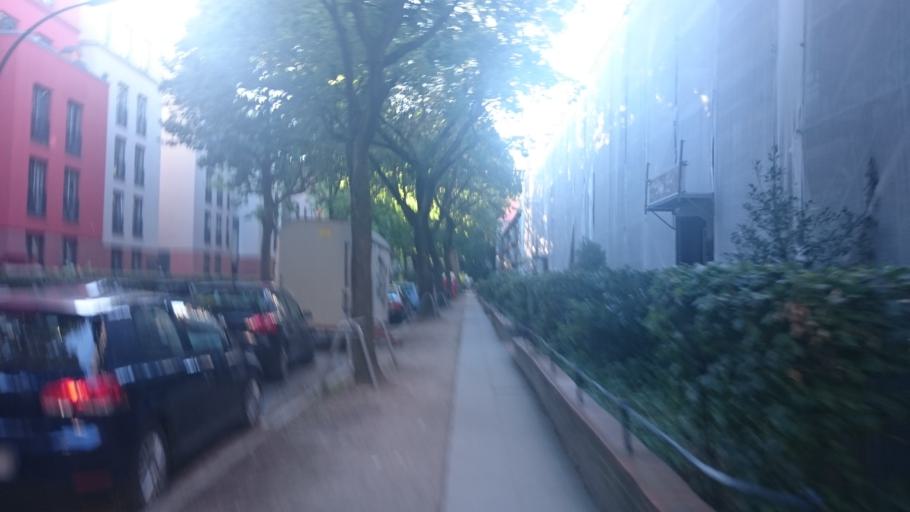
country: DE
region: Hamburg
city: Eimsbuettel
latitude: 53.5766
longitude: 9.9677
